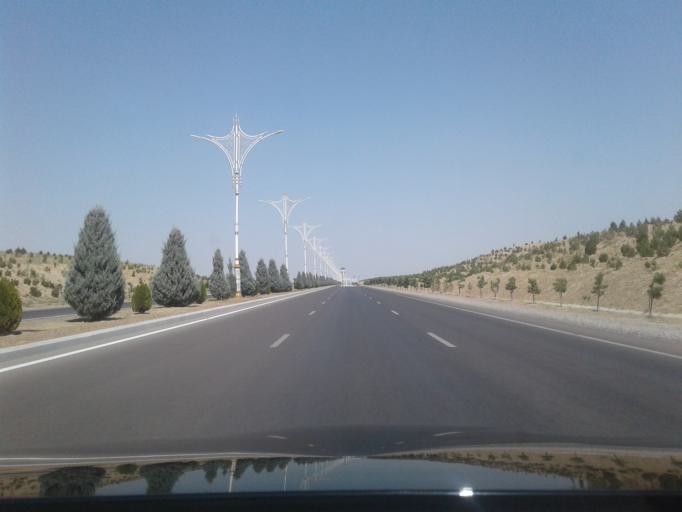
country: TM
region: Ahal
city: Ashgabat
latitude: 37.8785
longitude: 58.4067
